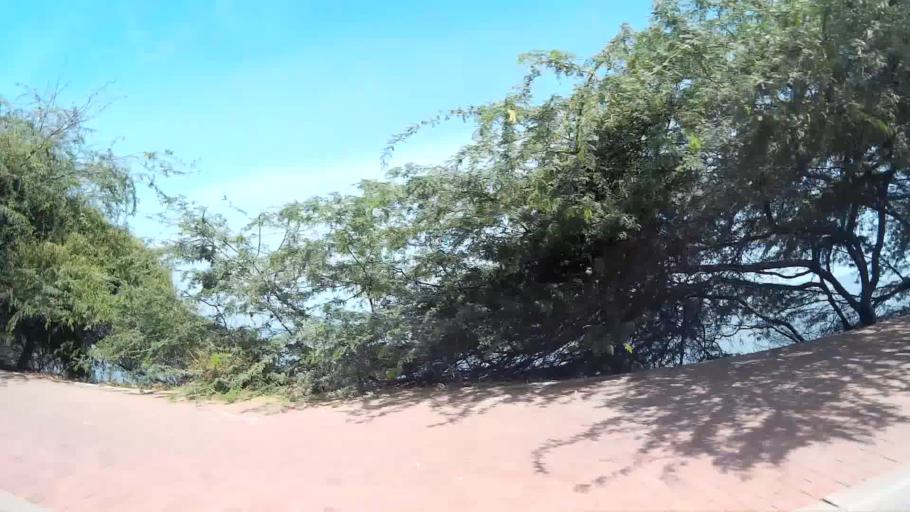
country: CO
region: Magdalena
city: Cienaga
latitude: 11.1236
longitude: -74.2313
